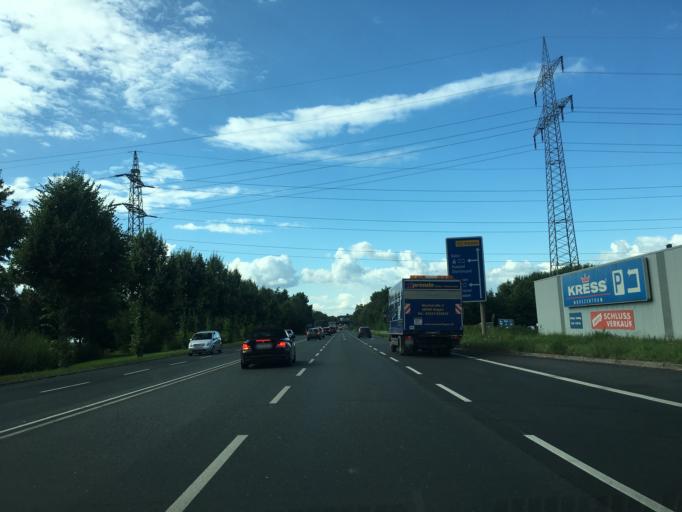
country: DE
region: North Rhine-Westphalia
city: Kamen
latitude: 51.5706
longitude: 7.6736
